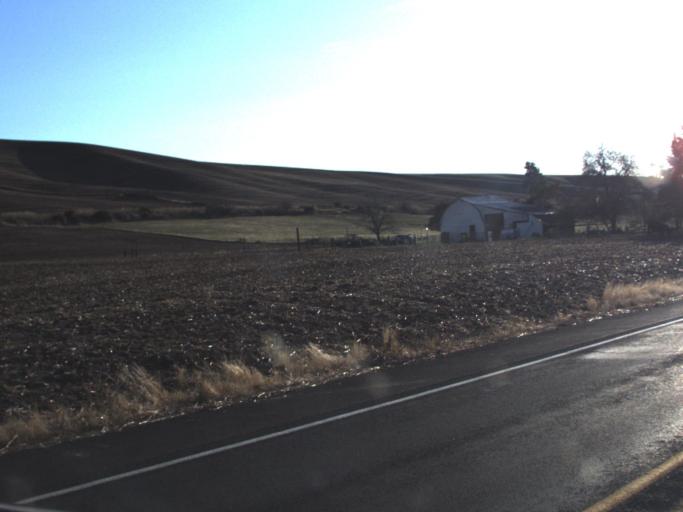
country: US
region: Washington
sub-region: Walla Walla County
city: Waitsburg
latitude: 46.1374
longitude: -118.1624
